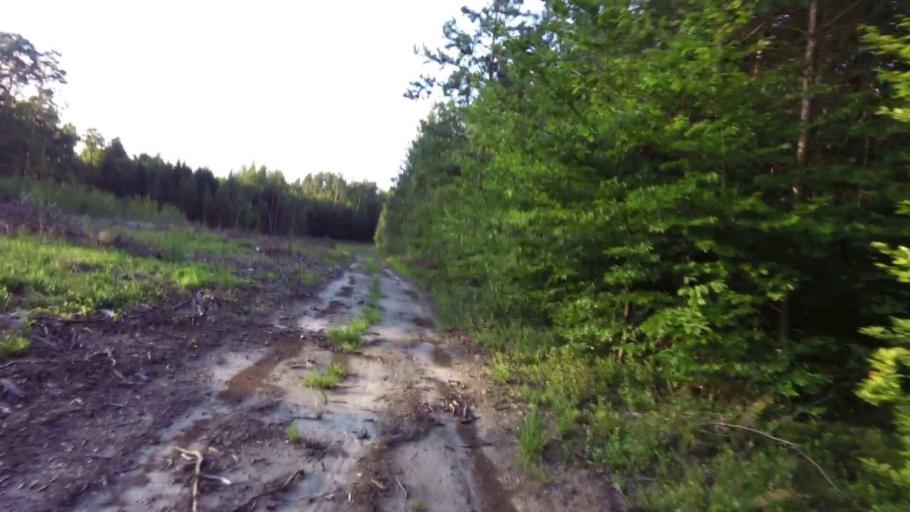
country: PL
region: West Pomeranian Voivodeship
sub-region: Powiat drawski
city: Zlocieniec
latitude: 53.5556
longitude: 16.0174
